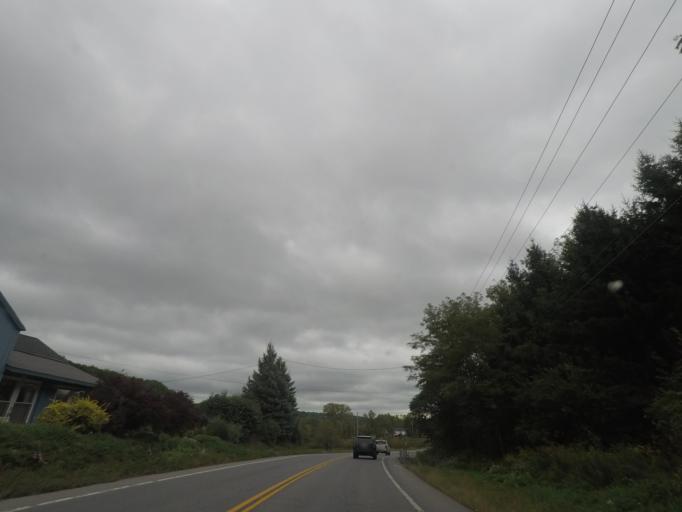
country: US
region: New York
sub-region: Saratoga County
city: Mechanicville
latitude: 42.9221
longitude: -73.7262
